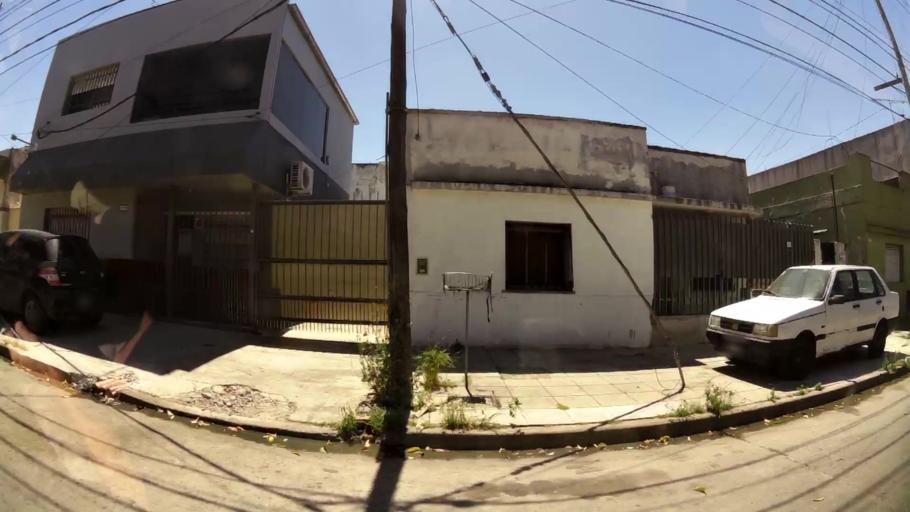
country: AR
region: Buenos Aires
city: Caseros
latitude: -34.5818
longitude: -58.5626
